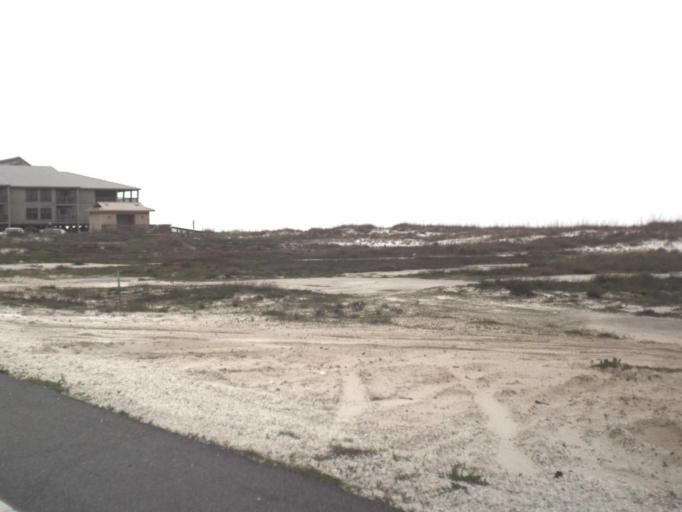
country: US
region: Alabama
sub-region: Baldwin County
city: Orange Beach
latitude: 30.2939
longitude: -87.4527
